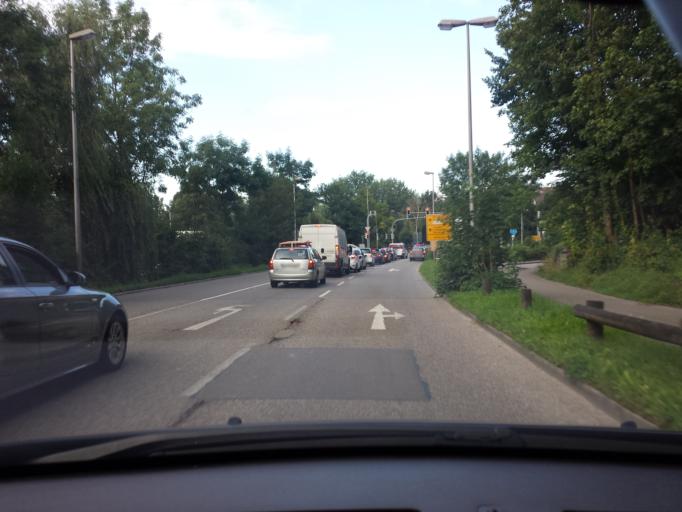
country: DE
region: Baden-Wuerttemberg
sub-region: Regierungsbezirk Stuttgart
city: Stuttgart Muehlhausen
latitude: 48.8715
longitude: 9.2720
